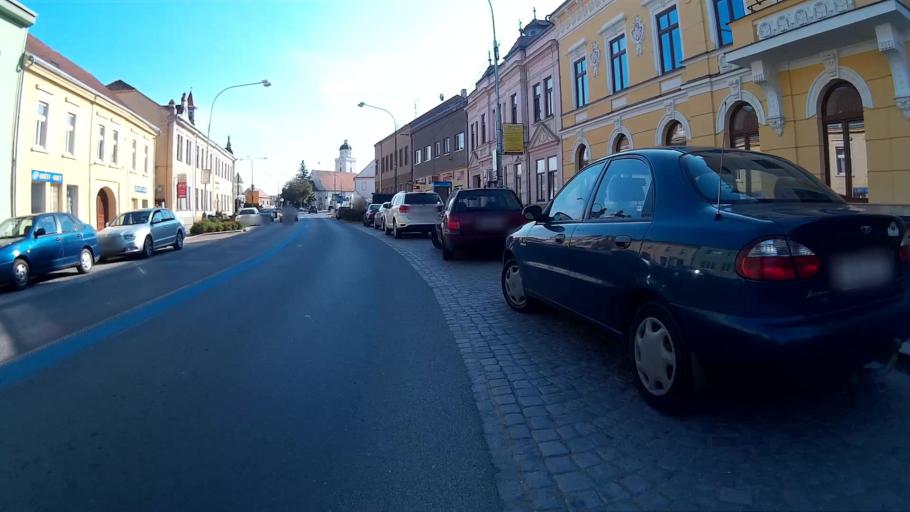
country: CZ
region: South Moravian
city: Pohorelice
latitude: 48.9824
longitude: 16.5250
